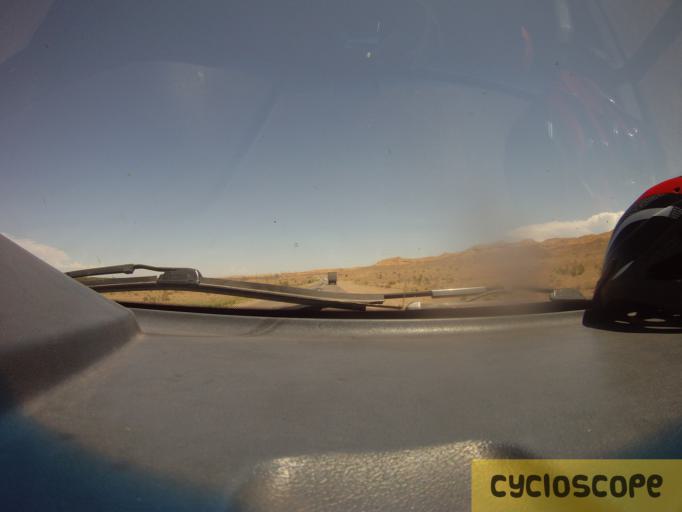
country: KZ
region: Almaty Oblysy
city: Kegen
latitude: 43.5304
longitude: 79.2894
